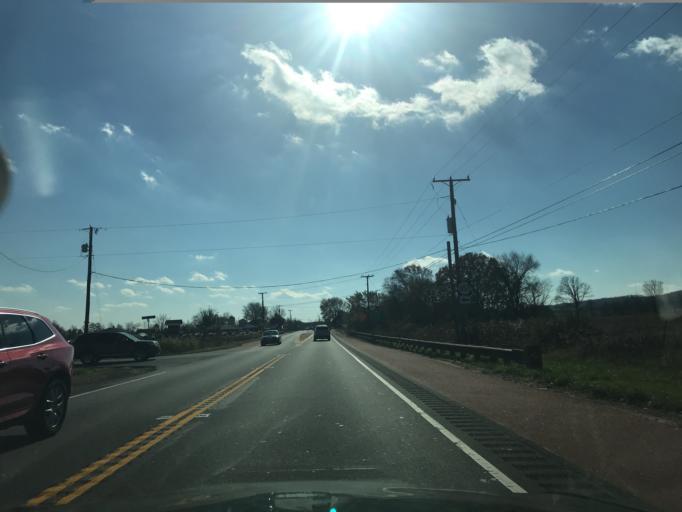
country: US
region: Maryland
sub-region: Frederick County
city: Point of Rocks
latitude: 39.2063
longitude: -77.5368
